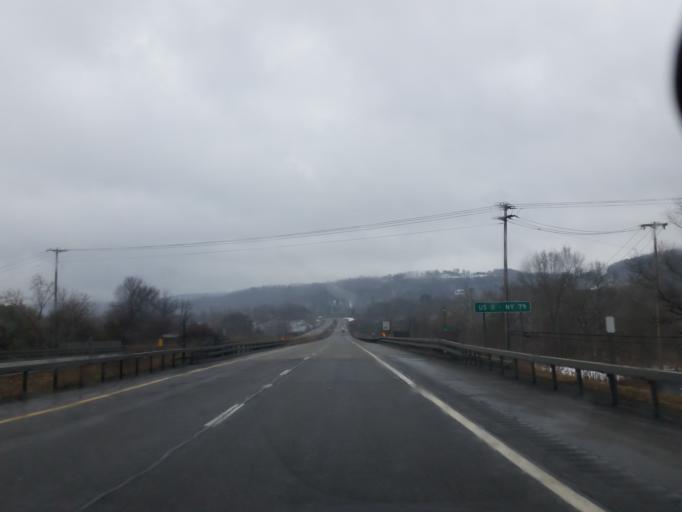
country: US
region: New York
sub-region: Chenango County
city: Lakeview
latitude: 42.3392
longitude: -75.9785
